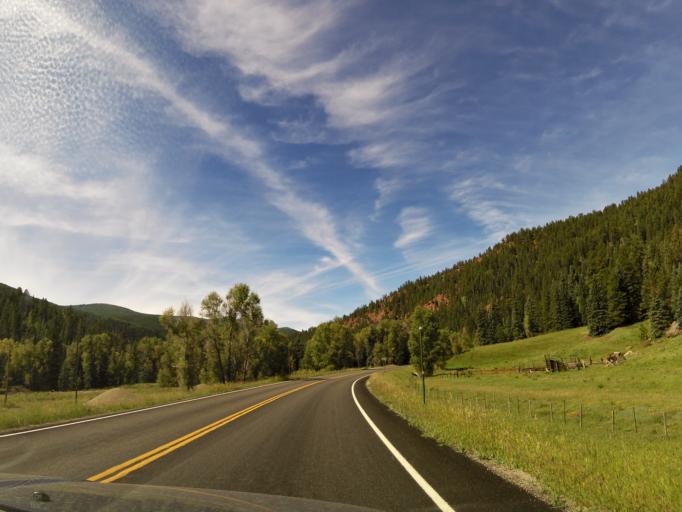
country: US
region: Colorado
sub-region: Montezuma County
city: Mancos
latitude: 37.6013
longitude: -108.1110
